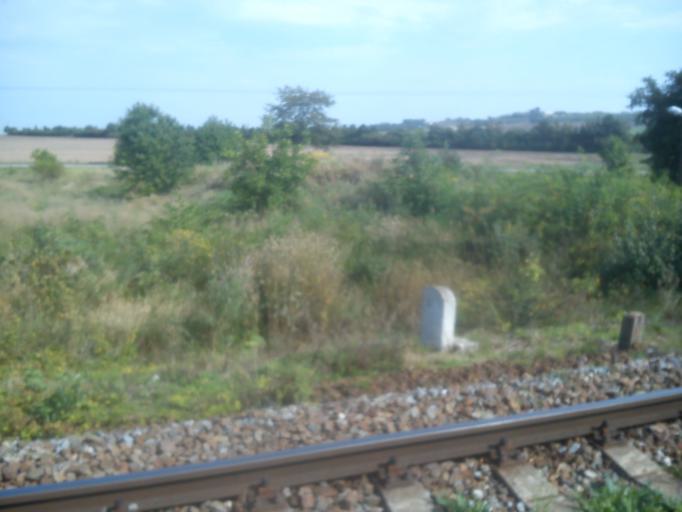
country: CZ
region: South Moravian
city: Sokolnice
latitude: 49.1072
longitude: 16.7437
